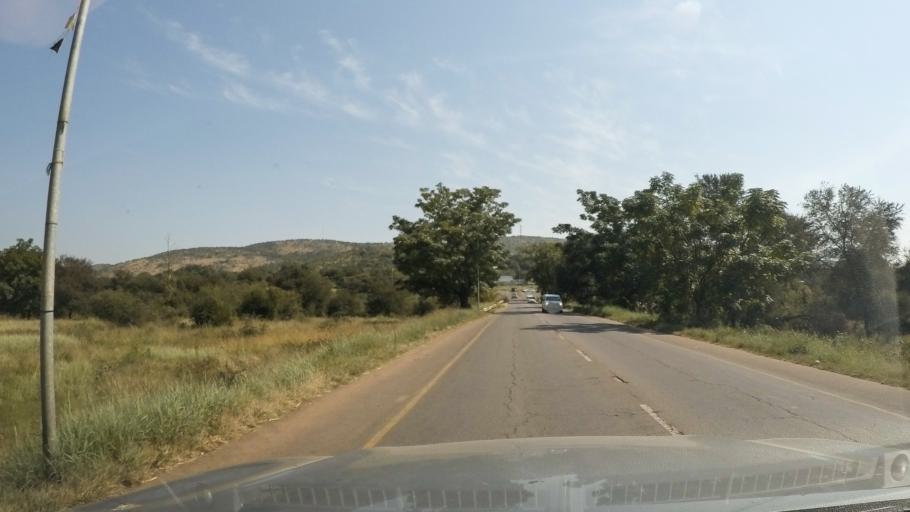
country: BW
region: South East
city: Lobatse
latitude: -25.2270
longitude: 25.6791
